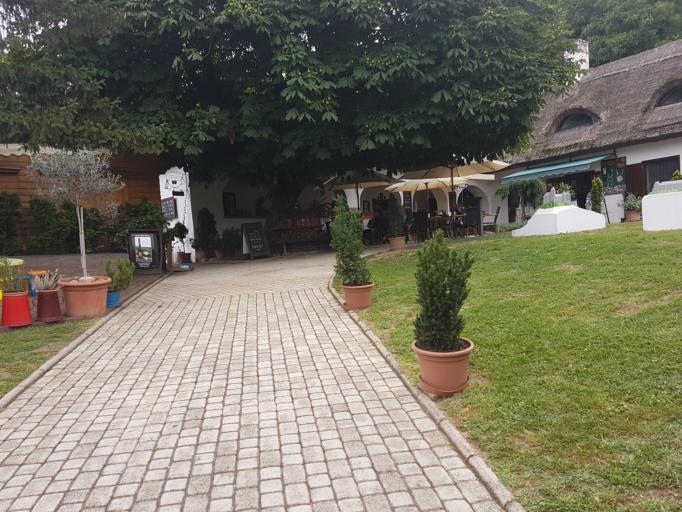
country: HU
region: Veszprem
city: Badacsonytomaj
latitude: 46.8028
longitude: 17.4351
